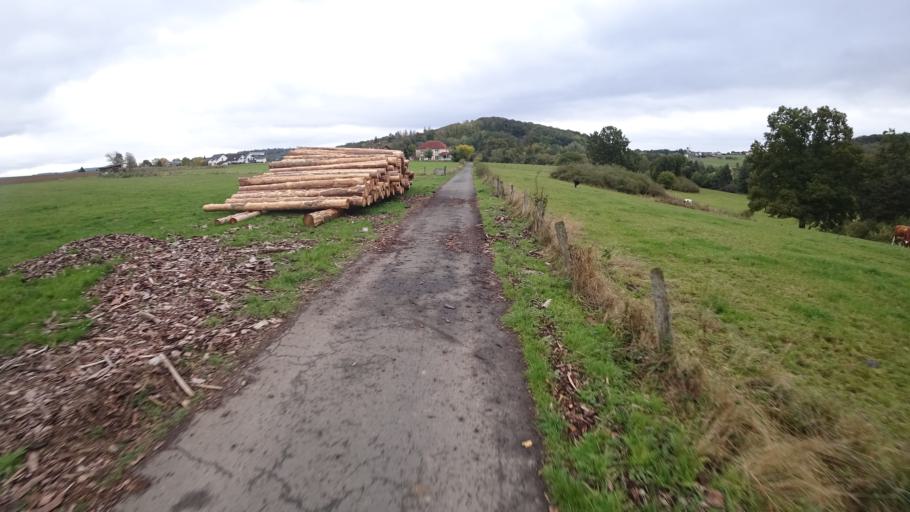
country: DE
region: Rheinland-Pfalz
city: Nordhofen
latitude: 50.5251
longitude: 7.7391
